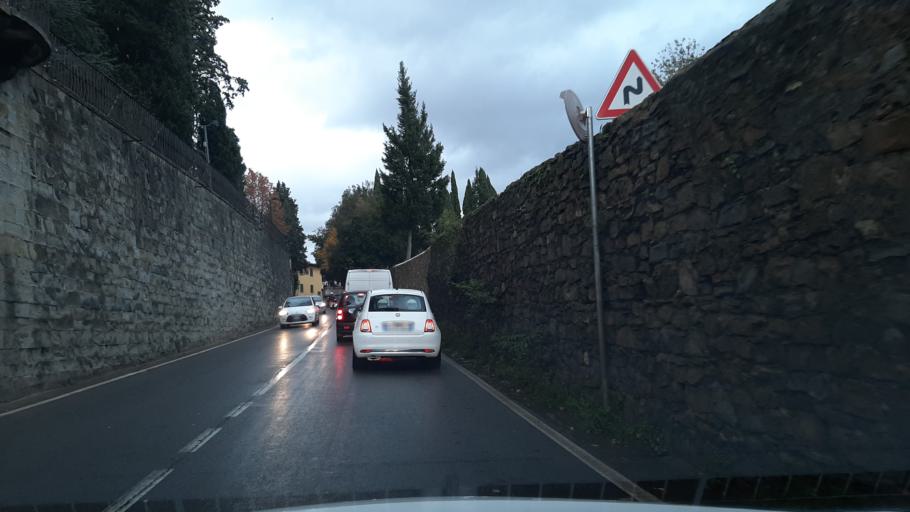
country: IT
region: Tuscany
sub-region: Province of Florence
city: Fiesole
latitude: 43.8020
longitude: 11.2679
